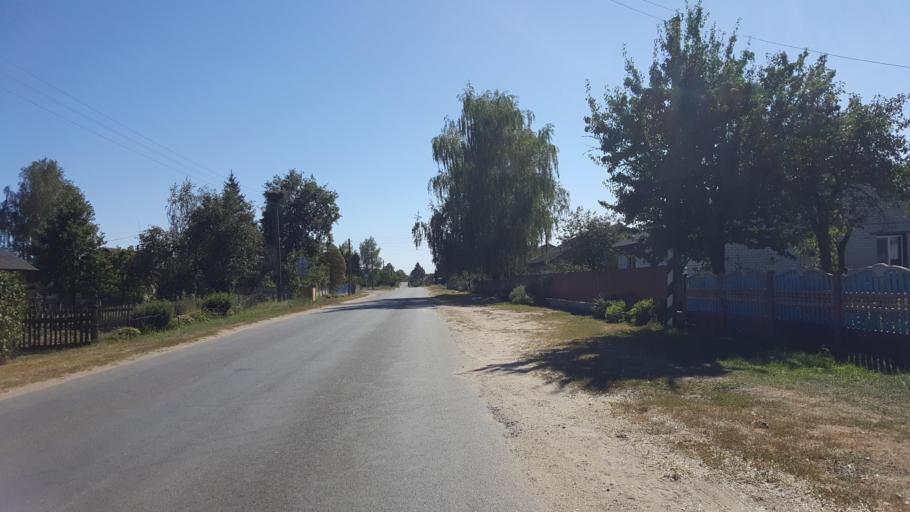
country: PL
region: Lublin Voivodeship
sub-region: Powiat bialski
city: Rokitno
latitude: 52.2421
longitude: 23.3386
